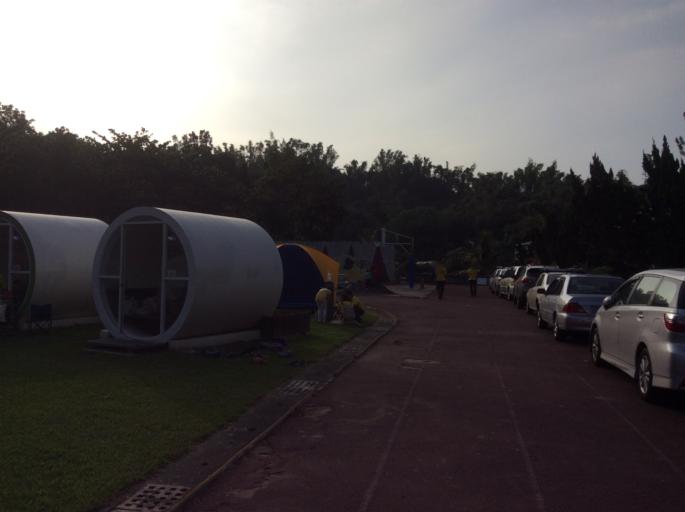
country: TW
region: Taiwan
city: Yujing
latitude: 23.0073
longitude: 120.4146
